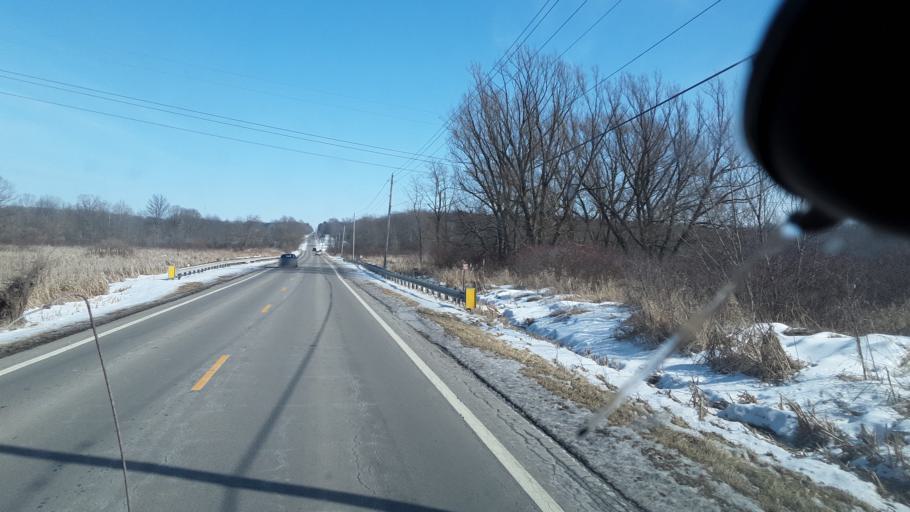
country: US
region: Ohio
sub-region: Columbiana County
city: Salem
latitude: 40.9442
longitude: -80.8325
